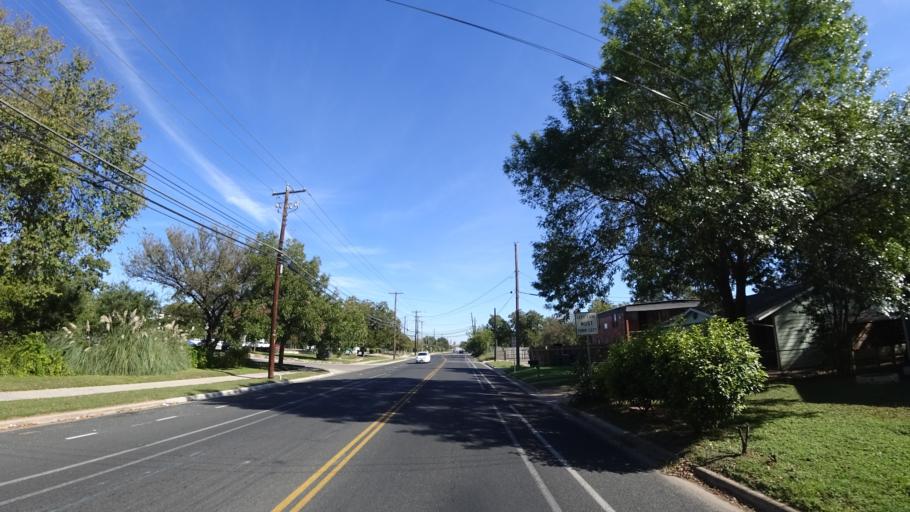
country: US
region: Texas
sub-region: Travis County
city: Austin
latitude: 30.2563
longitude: -97.6863
